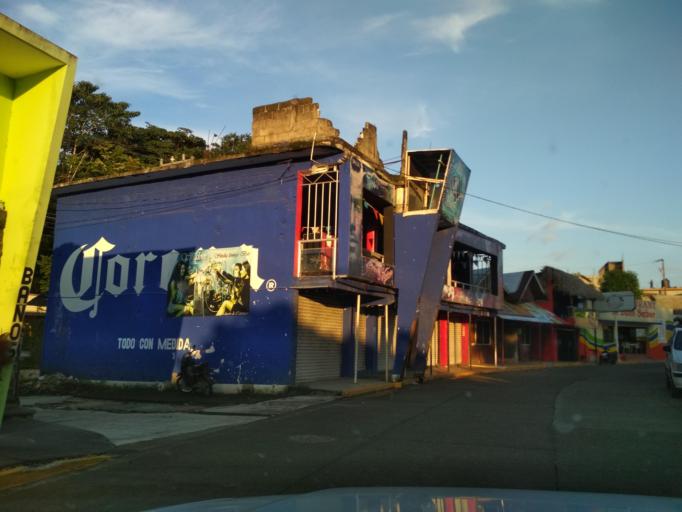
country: MX
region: Veracruz
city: Catemaco
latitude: 18.4173
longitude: -95.1102
